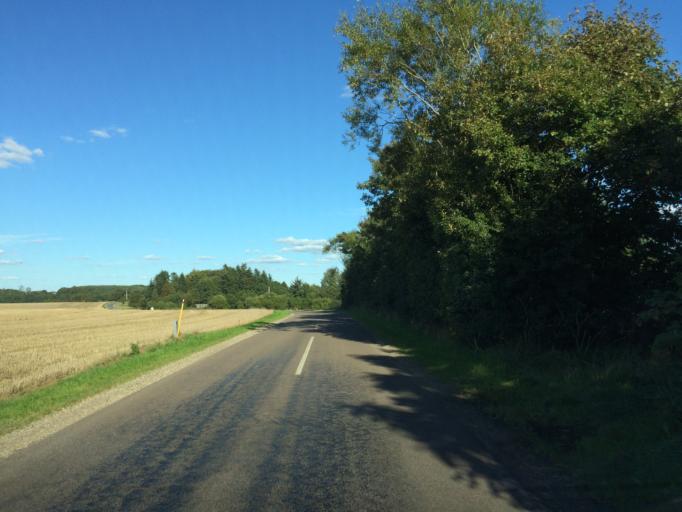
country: DK
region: Central Jutland
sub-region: Holstebro Kommune
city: Holstebro
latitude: 56.3180
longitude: 8.6290
